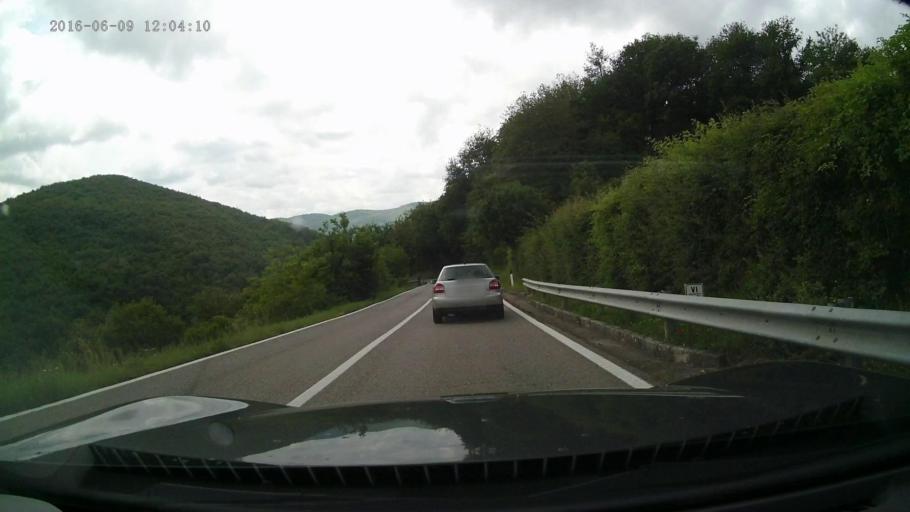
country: IT
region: Tuscany
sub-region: Province of Florence
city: Panzano in Chianti
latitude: 43.5228
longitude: 11.2988
